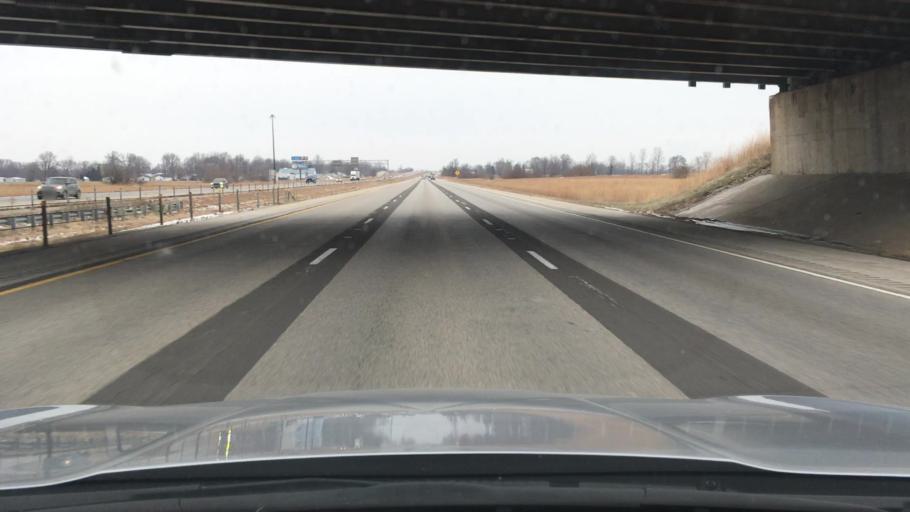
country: US
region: Illinois
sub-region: Sangamon County
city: Divernon
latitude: 39.6163
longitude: -89.6468
